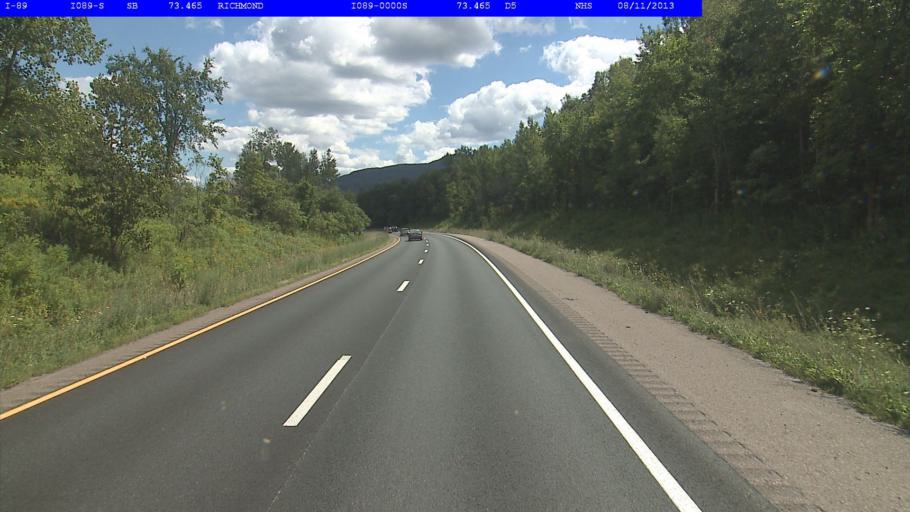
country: US
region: Vermont
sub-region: Chittenden County
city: Jericho
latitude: 44.3843
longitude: -72.9343
